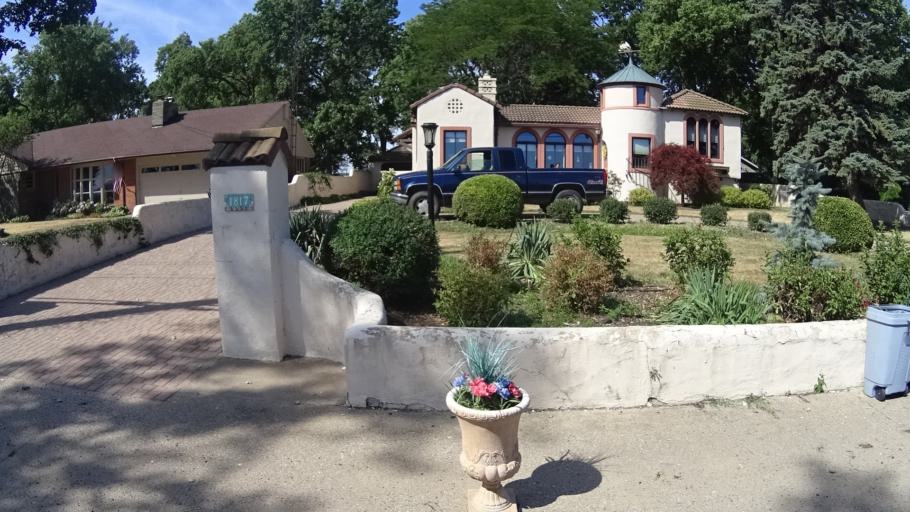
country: US
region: Ohio
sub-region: Erie County
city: Sandusky
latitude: 41.4675
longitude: -82.6655
